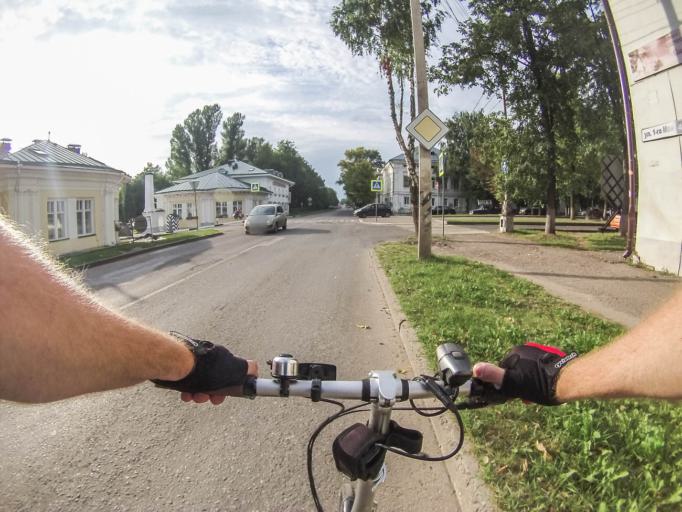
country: RU
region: Kostroma
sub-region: Kostromskoy Rayon
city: Kostroma
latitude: 57.7650
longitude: 40.9216
